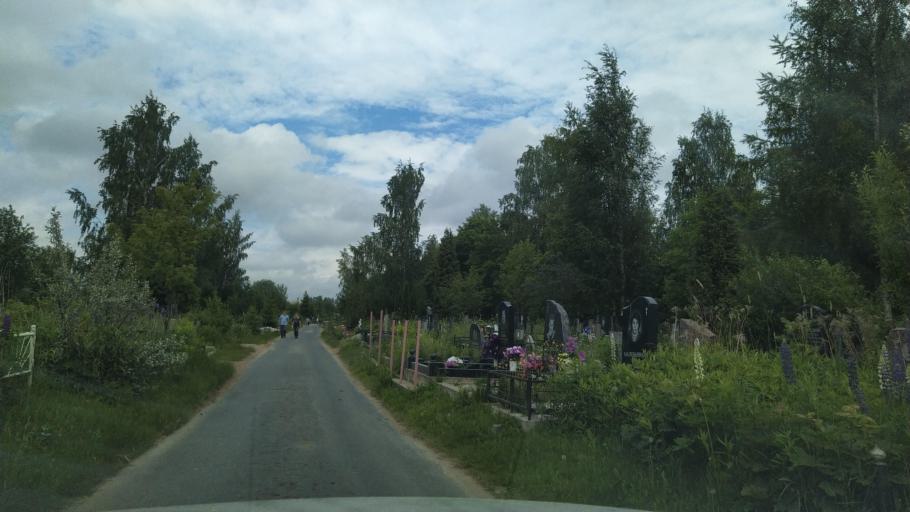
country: RU
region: St.-Petersburg
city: Pushkin
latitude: 59.6939
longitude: 30.3834
